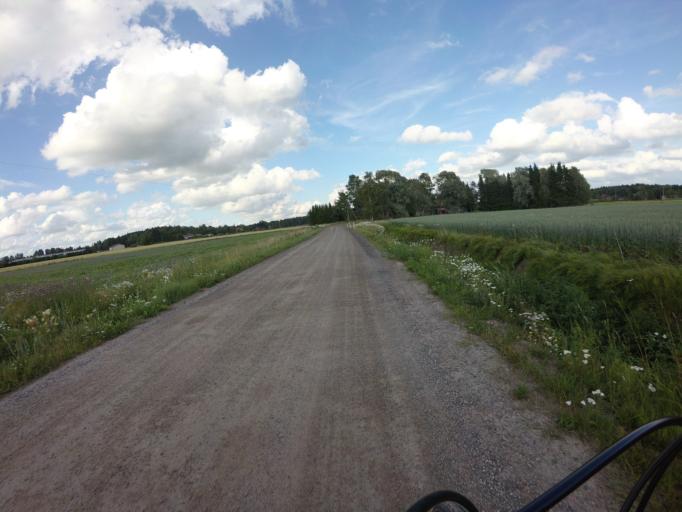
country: FI
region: Varsinais-Suomi
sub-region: Turku
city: Vahto
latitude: 60.5685
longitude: 22.3480
